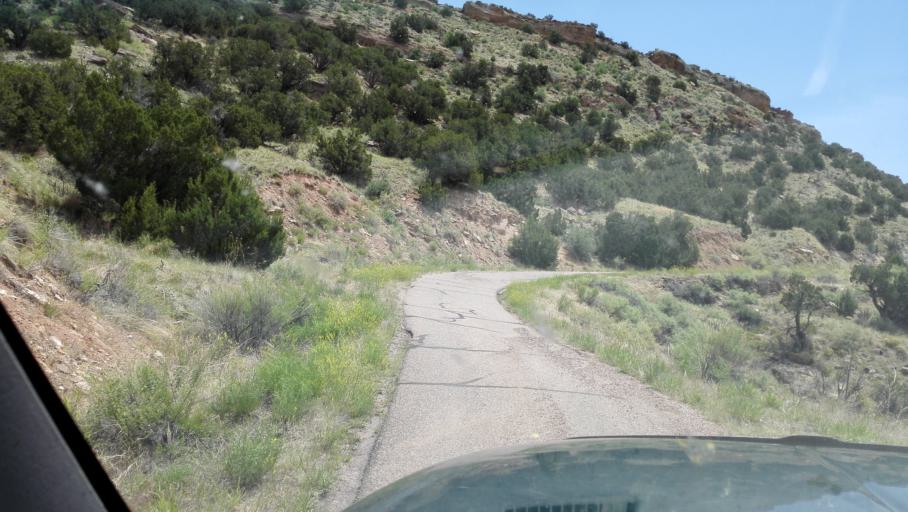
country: US
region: Colorado
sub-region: Fremont County
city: Canon City
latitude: 38.4721
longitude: -105.2567
